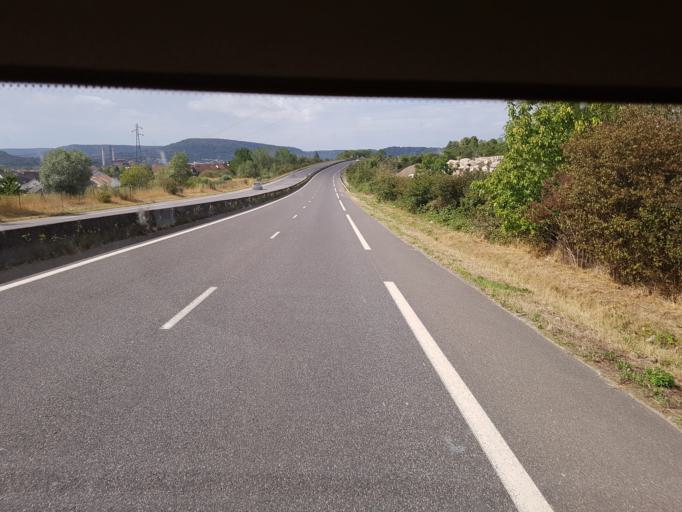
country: FR
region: Lorraine
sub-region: Departement de la Moselle
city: Gandrange
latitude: 49.2783
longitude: 6.1208
